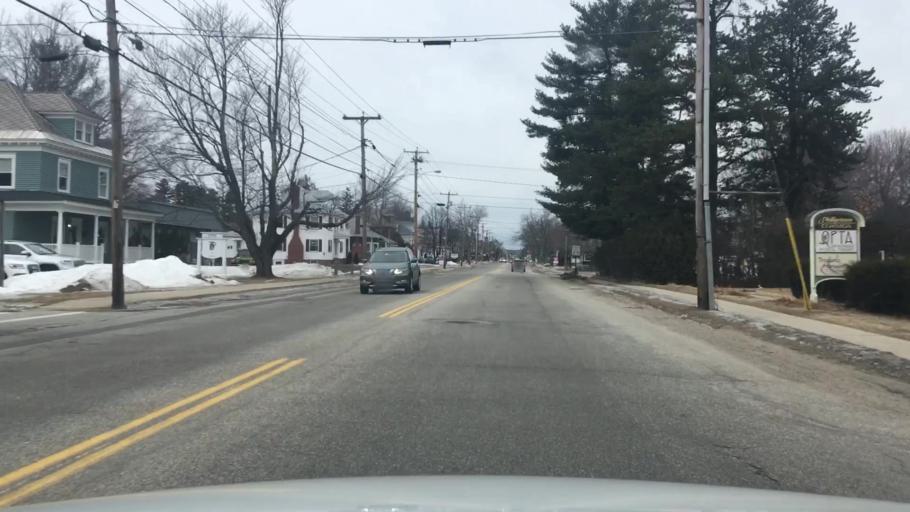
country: US
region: Maine
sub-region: York County
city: Sanford (historical)
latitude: 43.4284
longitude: -70.7676
